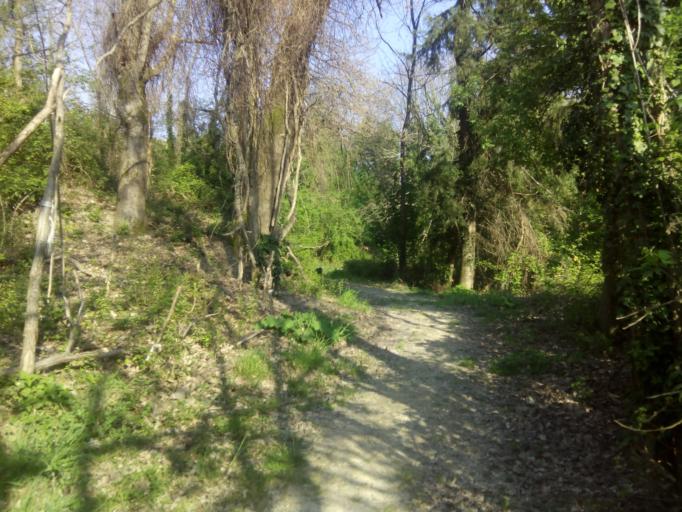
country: IT
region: Emilia-Romagna
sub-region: Provincia di Rimini
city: Mondaino
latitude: 43.8534
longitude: 12.6538
